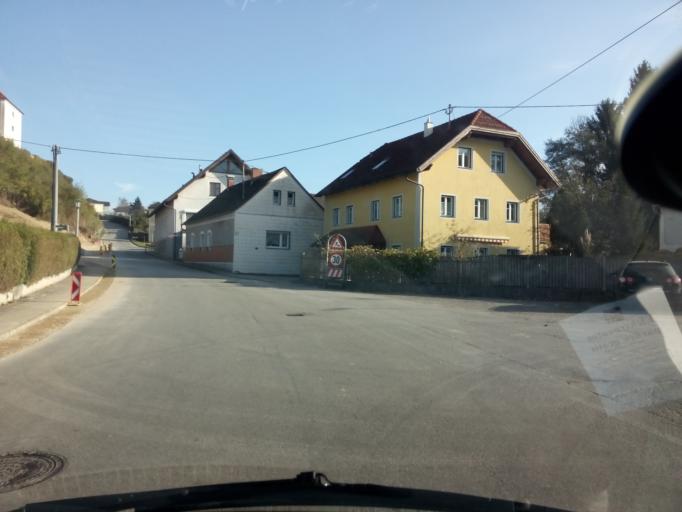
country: AT
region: Upper Austria
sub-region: Politischer Bezirk Kirchdorf an der Krems
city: Kremsmunster
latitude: 48.0541
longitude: 14.1436
